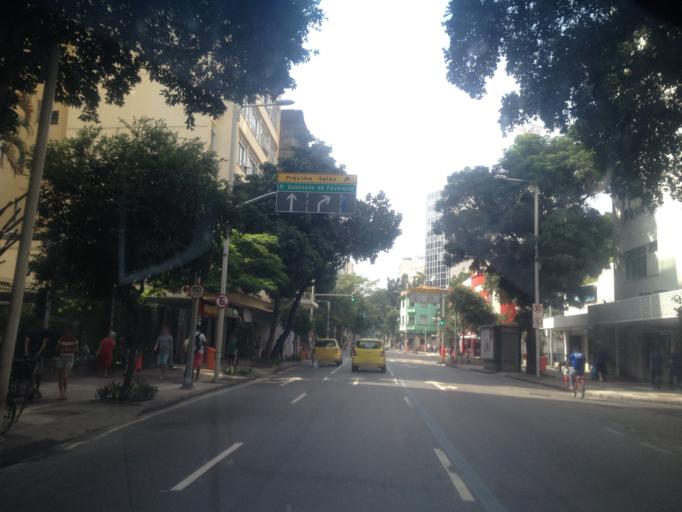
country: BR
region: Rio de Janeiro
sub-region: Rio De Janeiro
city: Rio de Janeiro
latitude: -22.9525
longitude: -43.1876
